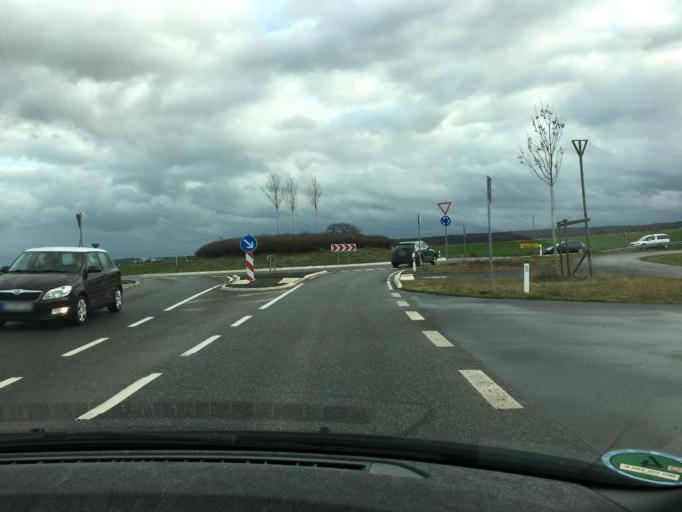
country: DE
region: North Rhine-Westphalia
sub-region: Regierungsbezirk Koln
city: Euskirchen
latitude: 50.6332
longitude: 6.7851
